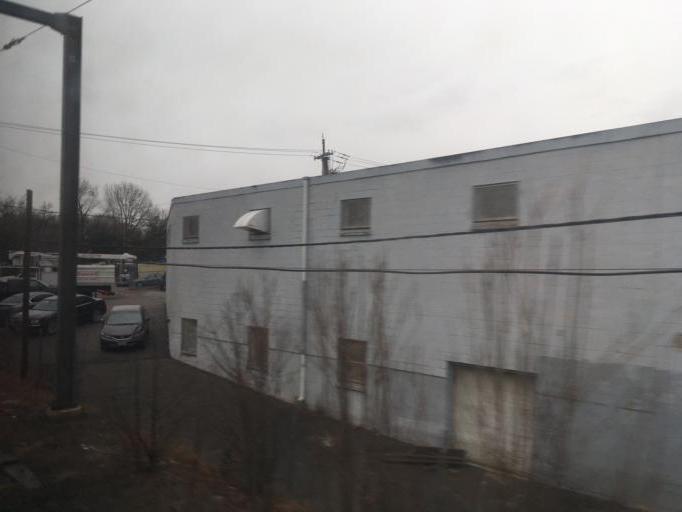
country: US
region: Massachusetts
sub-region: Norfolk County
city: Dedham
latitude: 42.2318
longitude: -71.1368
